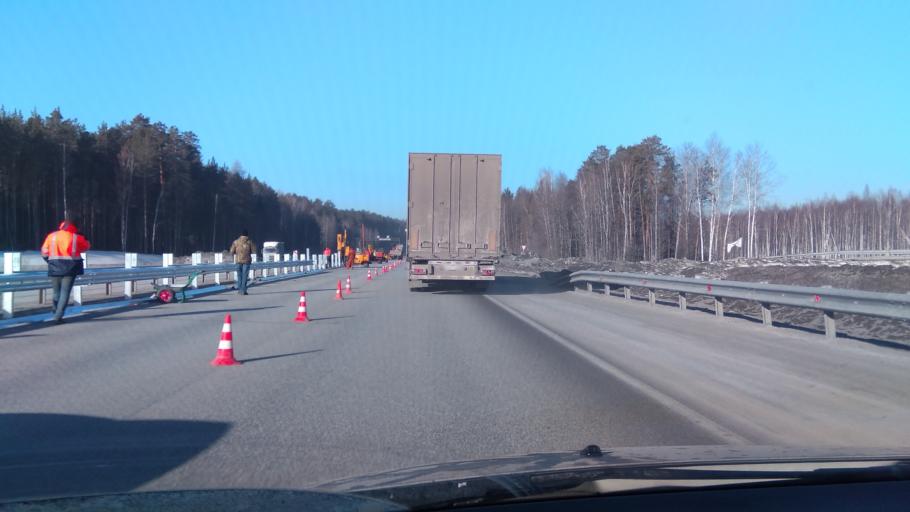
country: RU
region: Sverdlovsk
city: Severka
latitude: 56.8332
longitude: 60.3184
